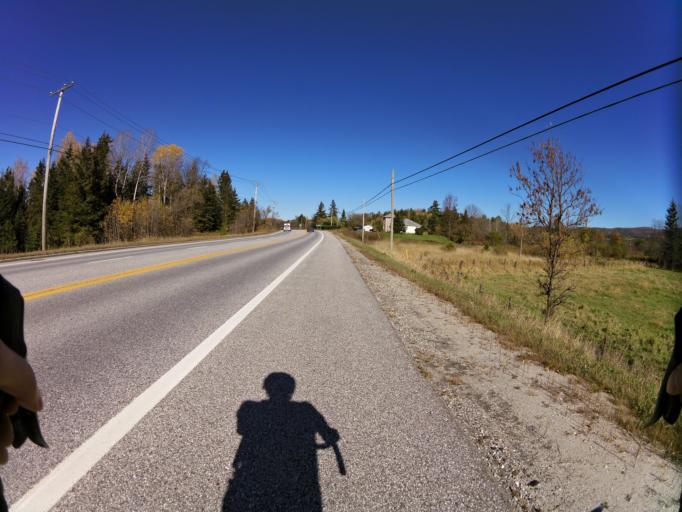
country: CA
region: Quebec
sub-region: Outaouais
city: Wakefield
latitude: 45.7988
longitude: -75.9454
